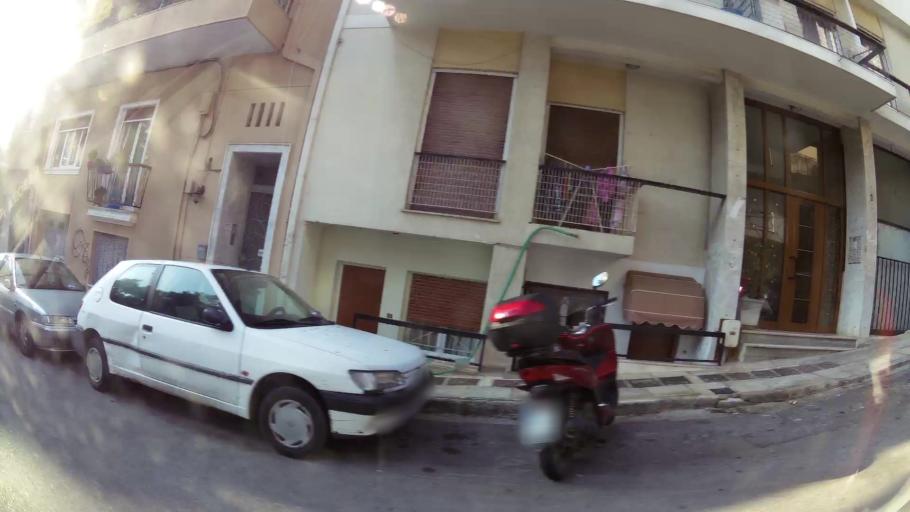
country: GR
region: Attica
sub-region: Nomarchia Athinas
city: Kaisariani
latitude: 37.9757
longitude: 23.7584
